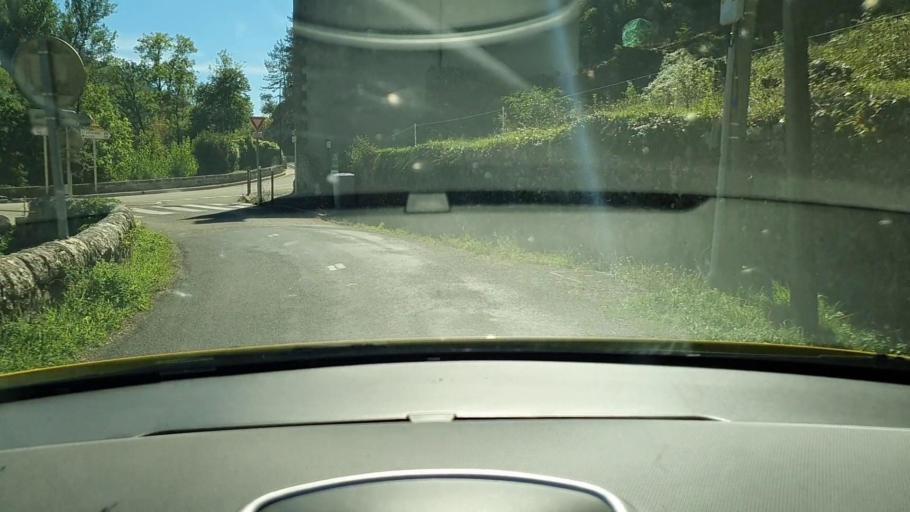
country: FR
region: Languedoc-Roussillon
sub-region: Departement du Gard
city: Le Vigan
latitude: 43.9661
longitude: 3.4370
